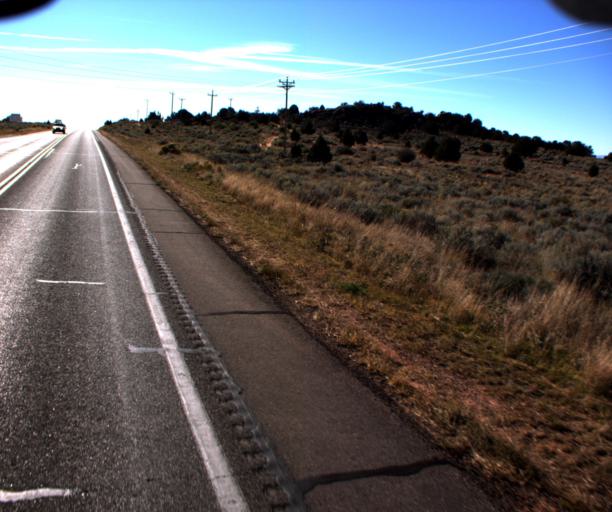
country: US
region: Arizona
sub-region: Mohave County
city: Colorado City
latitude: 36.9706
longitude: -112.9751
